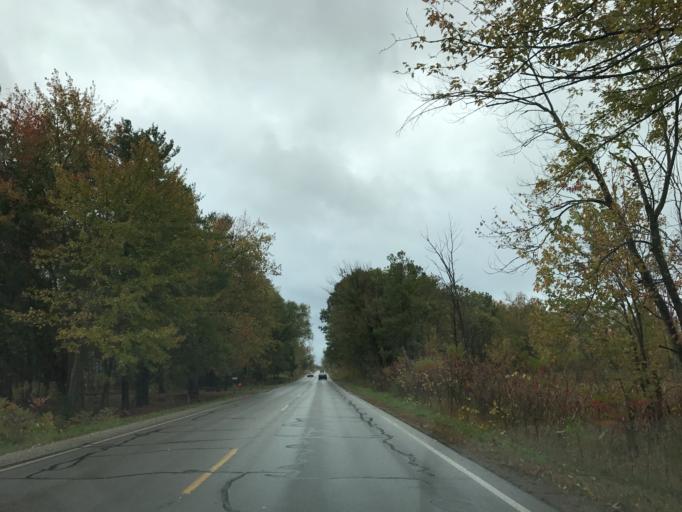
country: US
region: Michigan
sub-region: Oakland County
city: South Lyon
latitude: 42.4099
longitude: -83.6462
